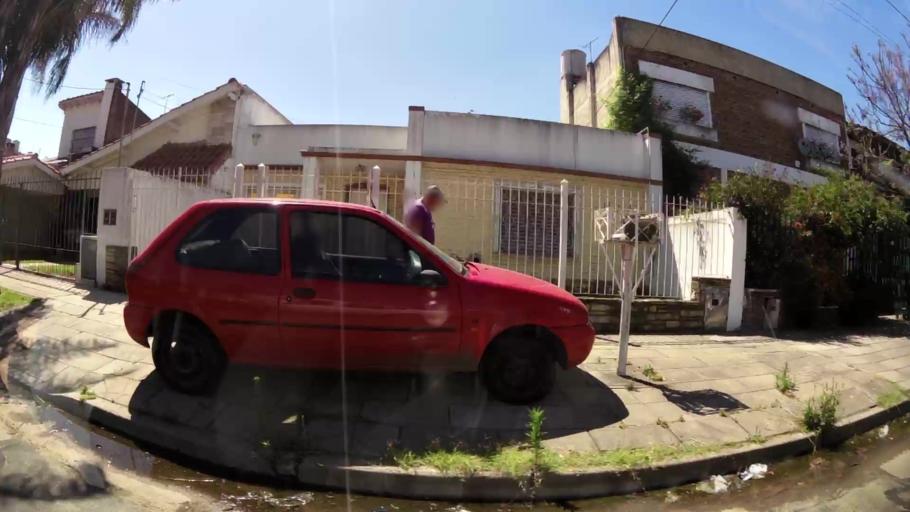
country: AR
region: Buenos Aires
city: Ituzaingo
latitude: -34.6589
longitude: -58.6487
